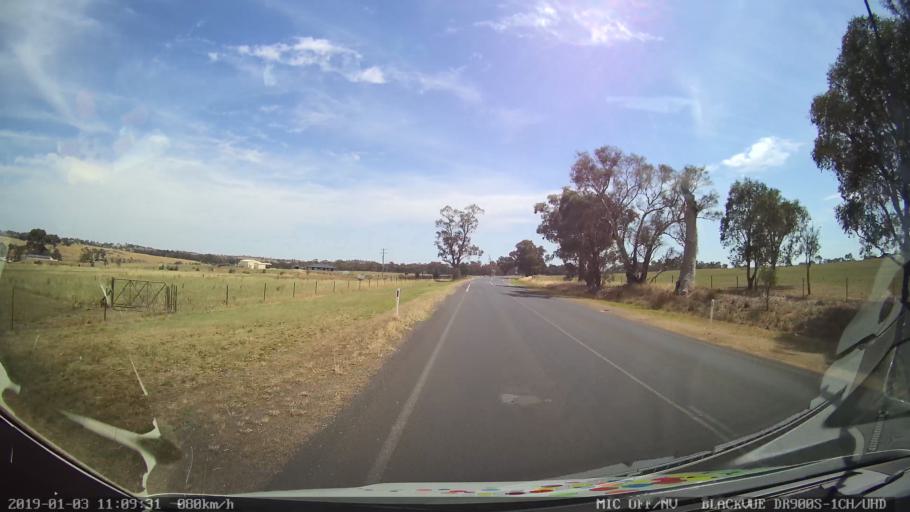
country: AU
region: New South Wales
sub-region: Young
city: Young
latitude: -34.2374
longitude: 148.2555
